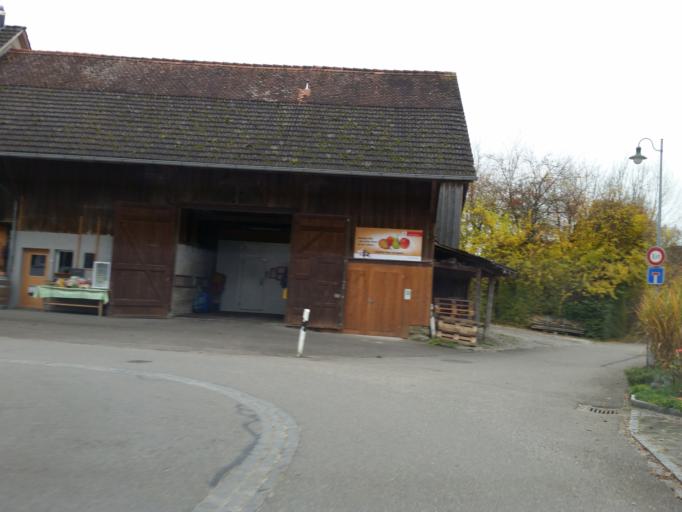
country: CH
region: Thurgau
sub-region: Arbon District
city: Amriswil
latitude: 47.5593
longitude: 9.3223
